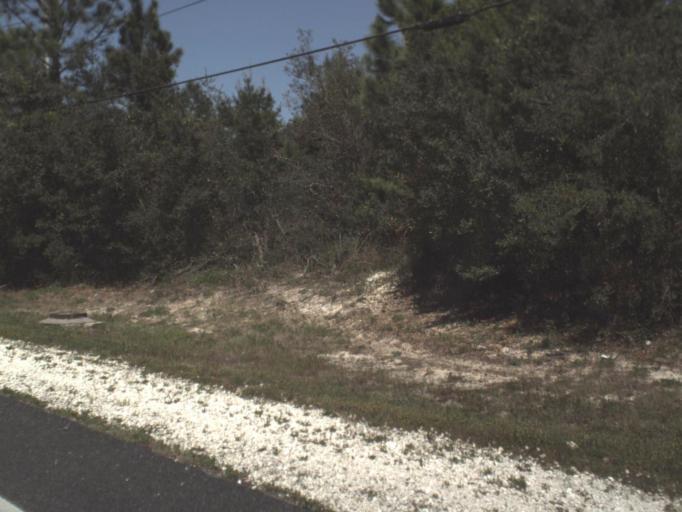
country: US
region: Florida
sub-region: Okaloosa County
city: Mary Esther
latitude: 30.4121
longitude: -86.7362
